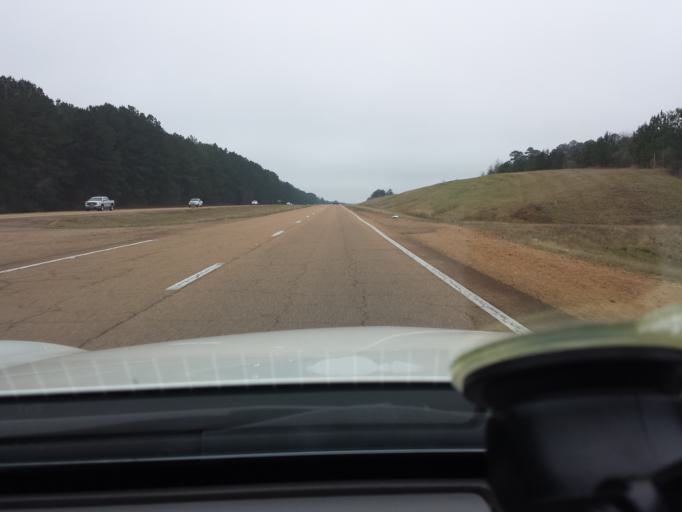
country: US
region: Mississippi
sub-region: Winston County
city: Louisville
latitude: 33.0996
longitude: -89.0853
